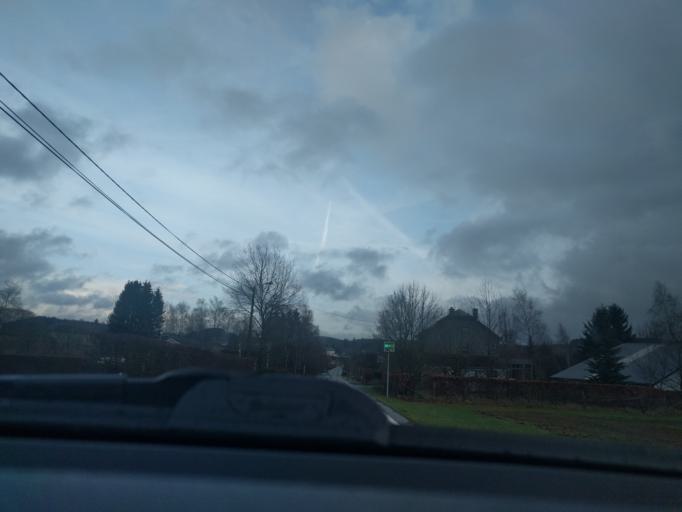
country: BE
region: Wallonia
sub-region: Province du Luxembourg
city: Gouvy
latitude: 50.1875
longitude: 5.9686
